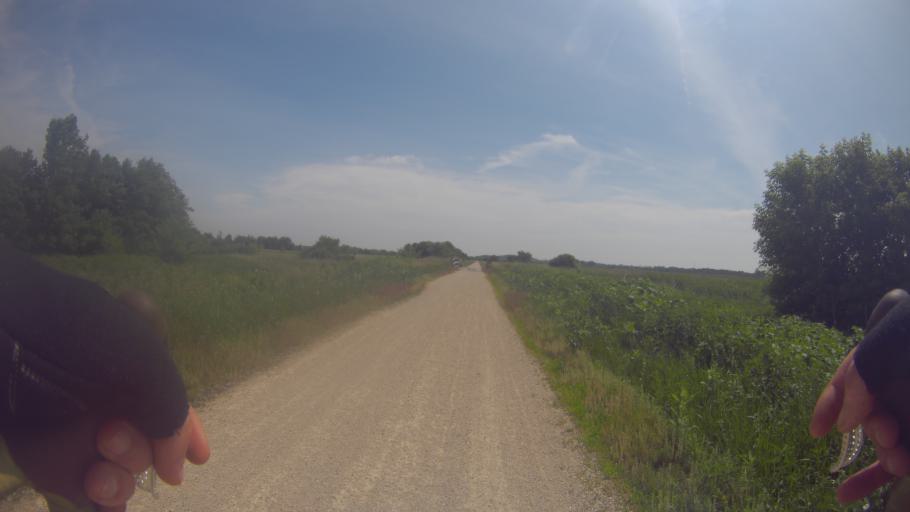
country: US
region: Wisconsin
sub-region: Jefferson County
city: Lake Ripley
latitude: 43.0553
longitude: -88.9885
